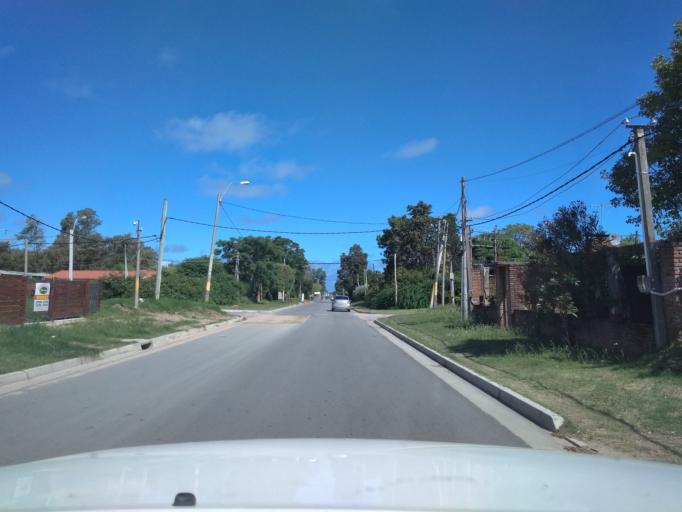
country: UY
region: Canelones
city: Colonia Nicolich
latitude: -34.8237
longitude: -55.9724
